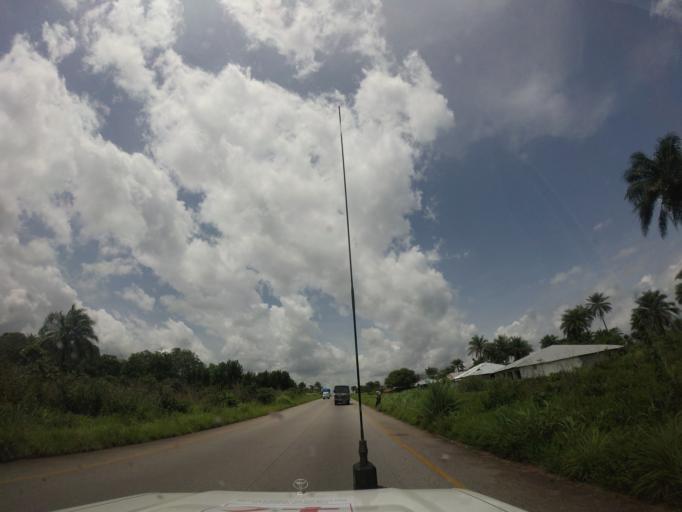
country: SL
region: Northern Province
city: Rokupr
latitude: 8.4822
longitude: -12.4343
